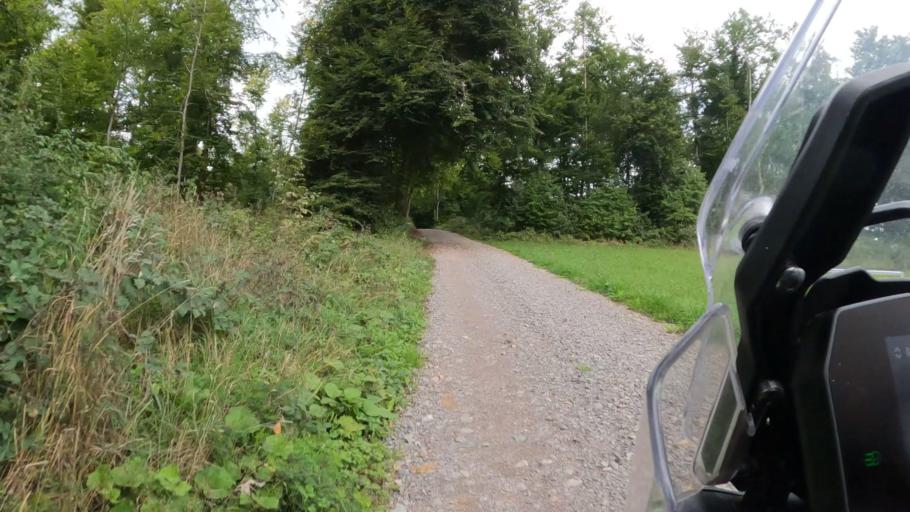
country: DE
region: Baden-Wuerttemberg
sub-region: Freiburg Region
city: Eggingen
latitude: 47.7068
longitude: 8.3643
